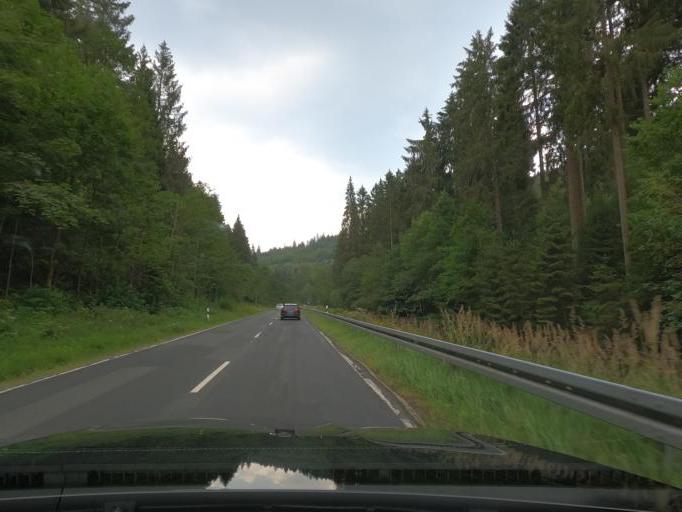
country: DE
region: Lower Saxony
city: Wildemann
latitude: 51.8377
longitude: 10.2641
